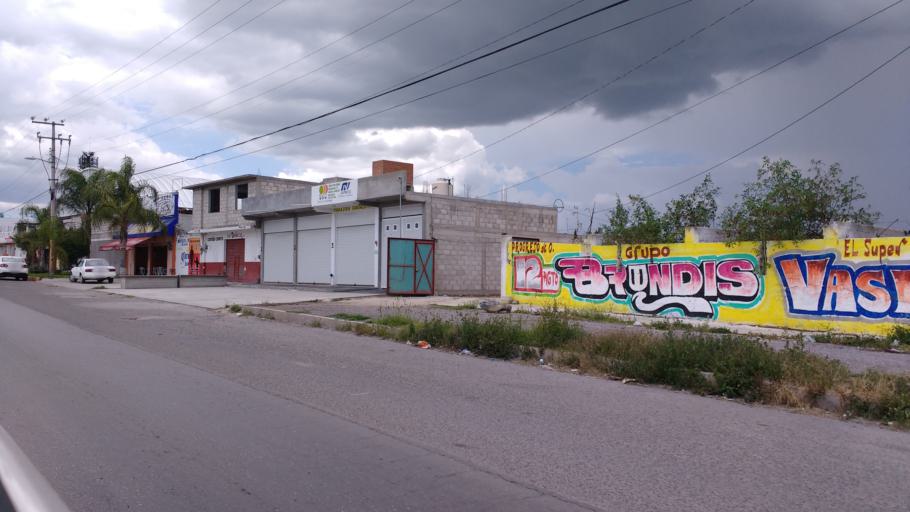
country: MX
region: Hidalgo
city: Tlahuelilpan
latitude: 20.1411
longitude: -99.2349
